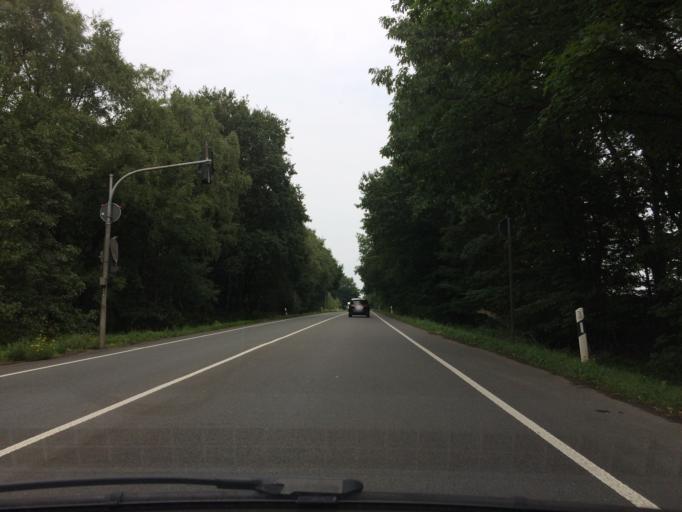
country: DE
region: North Rhine-Westphalia
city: Dorsten
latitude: 51.7023
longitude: 6.9346
